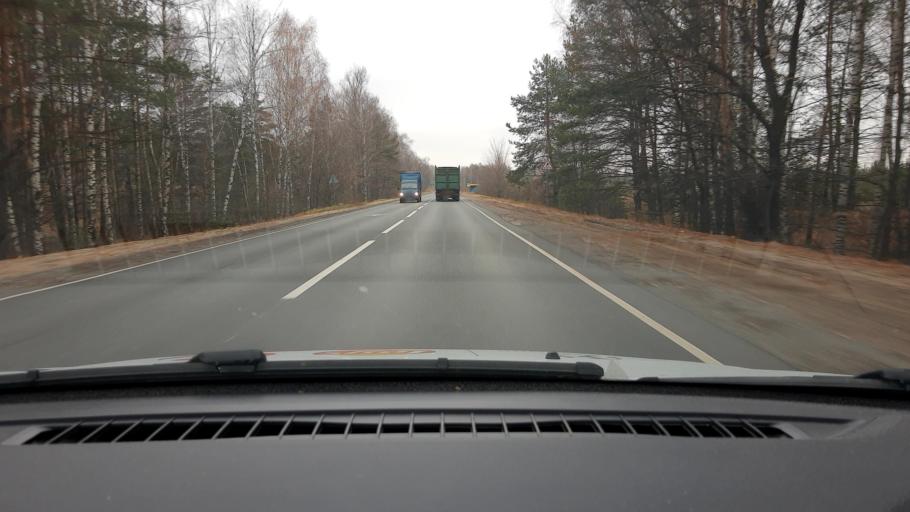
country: RU
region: Nizjnij Novgorod
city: Gorodets
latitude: 56.5621
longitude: 43.4932
